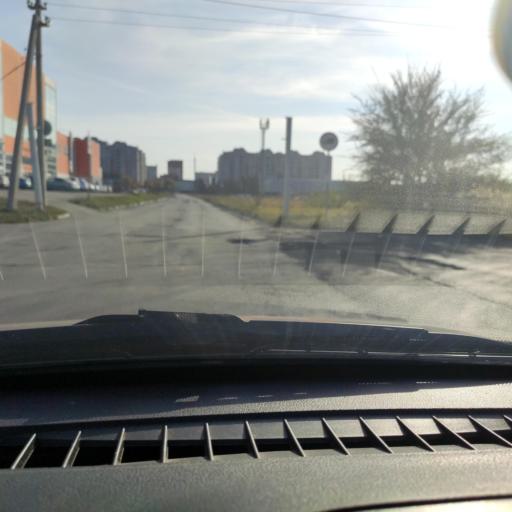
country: RU
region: Samara
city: Tol'yatti
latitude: 53.5533
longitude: 49.3236
